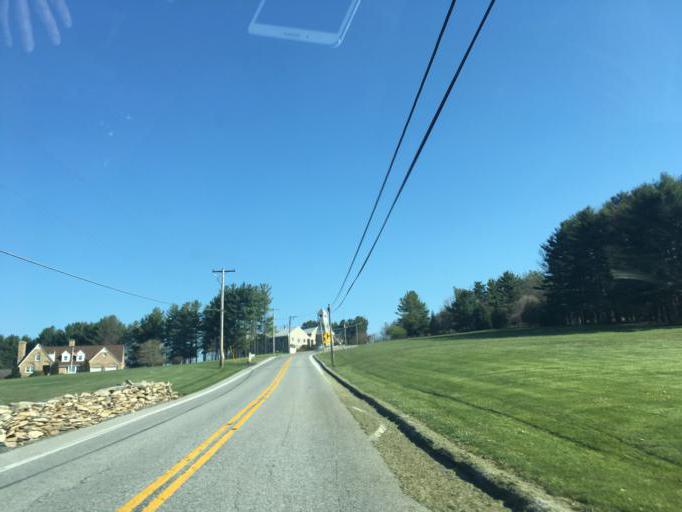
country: US
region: Maryland
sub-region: Washington County
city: Cavetown
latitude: 39.5806
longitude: -77.5567
